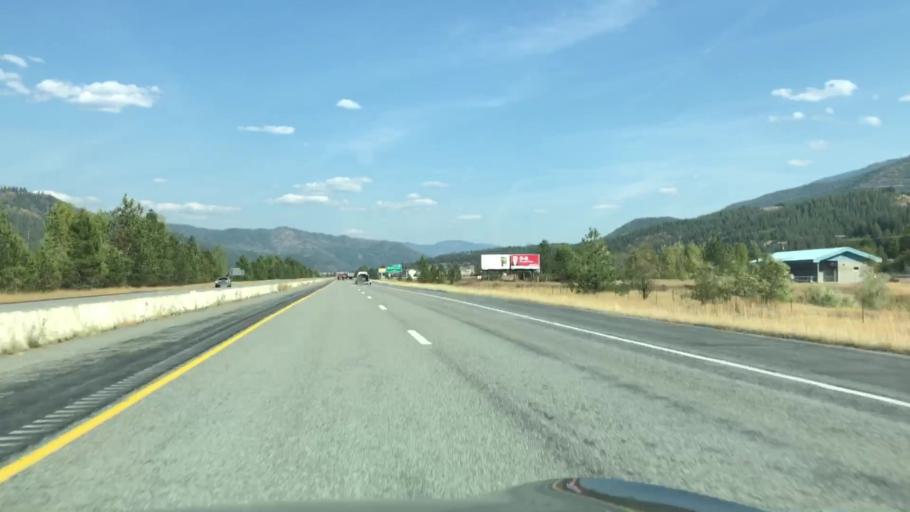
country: US
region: Idaho
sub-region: Shoshone County
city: Pinehurst
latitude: 47.5461
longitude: -116.2057
